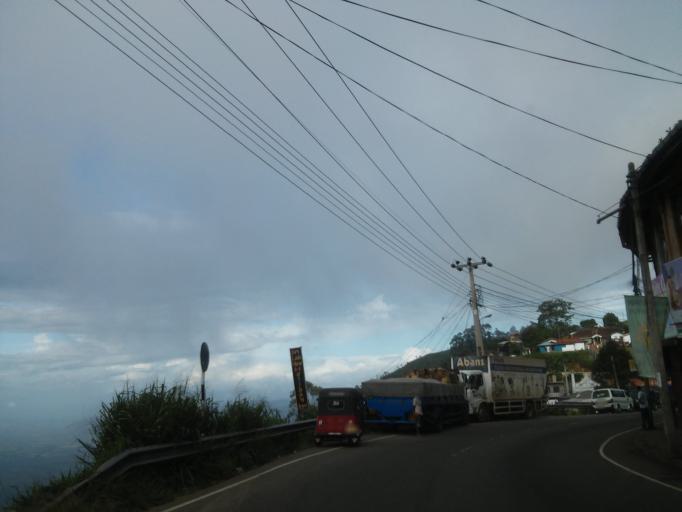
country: LK
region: Uva
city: Haputale
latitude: 6.7683
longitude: 80.9597
